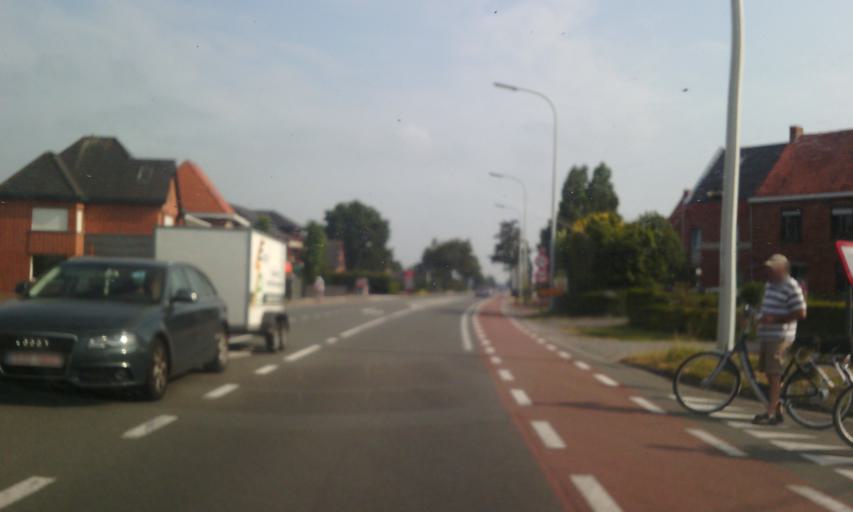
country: BE
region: Flanders
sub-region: Provincie Oost-Vlaanderen
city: Waarschoot
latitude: 51.1291
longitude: 3.6075
